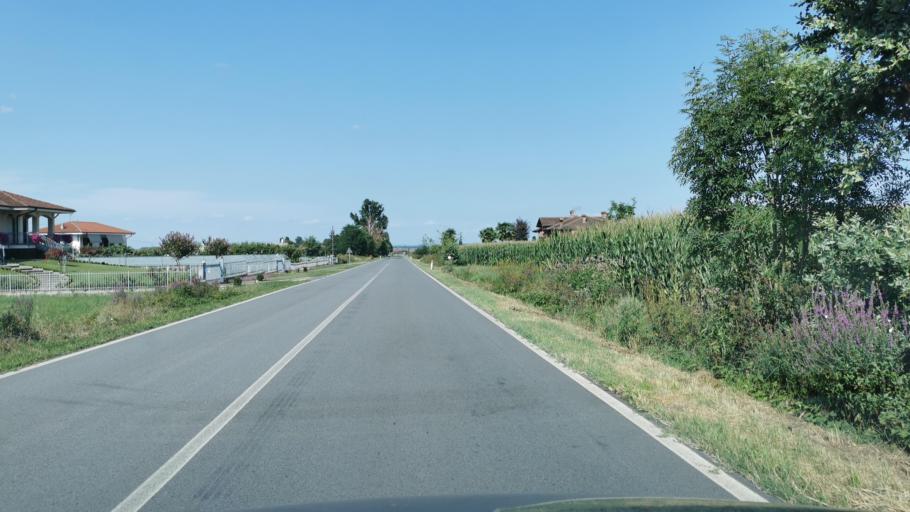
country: IT
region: Piedmont
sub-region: Provincia di Cuneo
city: Revello
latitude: 44.6737
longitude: 7.4042
